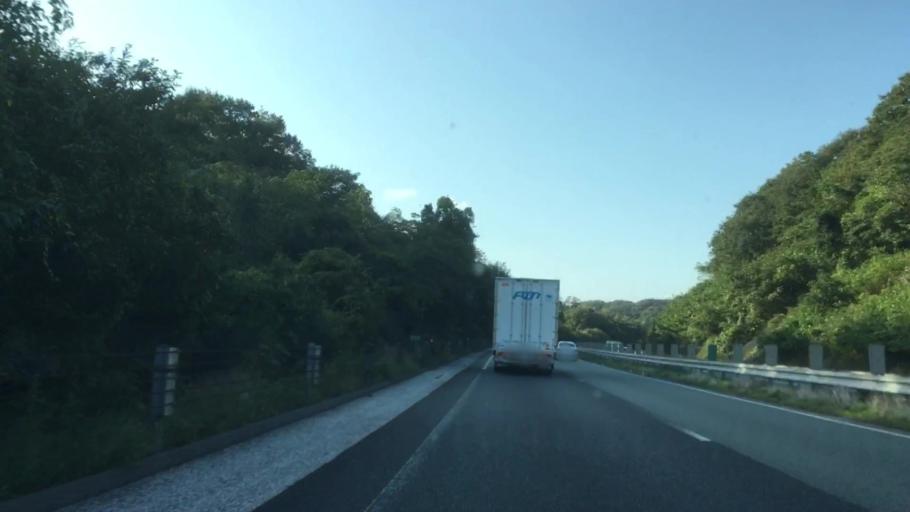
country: JP
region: Yamaguchi
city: Ogori-shimogo
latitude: 34.1613
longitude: 131.3289
